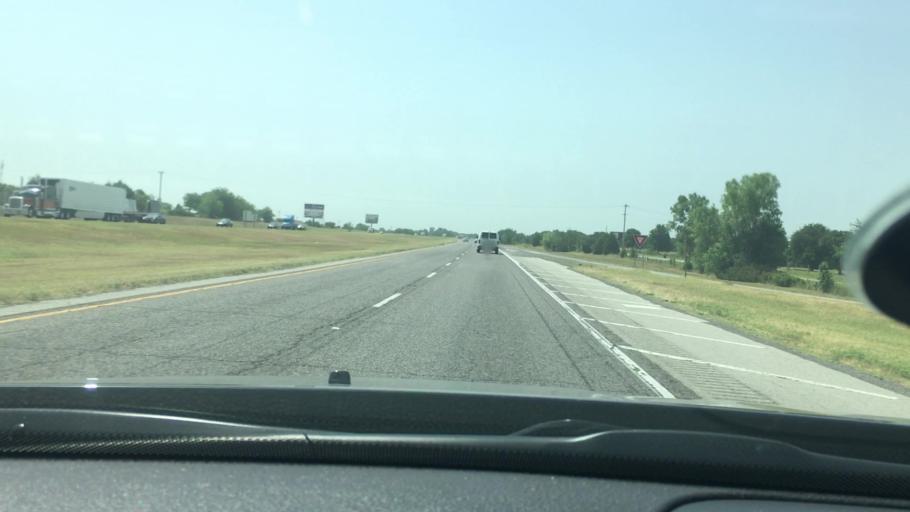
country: US
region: Oklahoma
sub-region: Garvin County
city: Wynnewood
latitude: 34.5689
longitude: -97.1980
